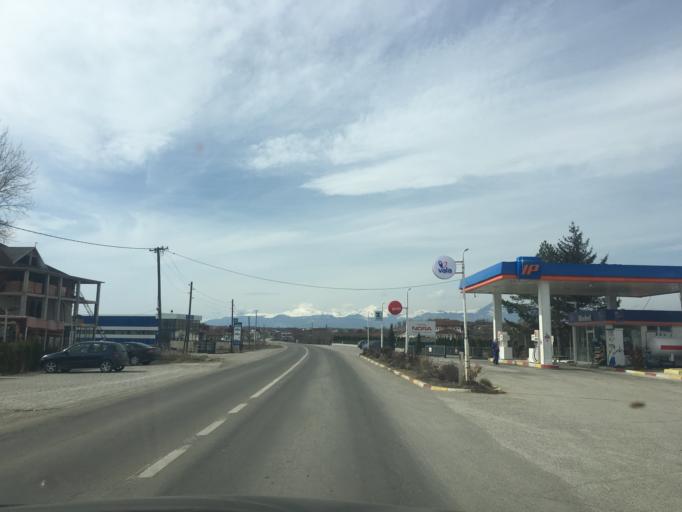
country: XK
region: Pec
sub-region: Komuna e Klines
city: Klina
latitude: 42.5928
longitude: 20.5690
